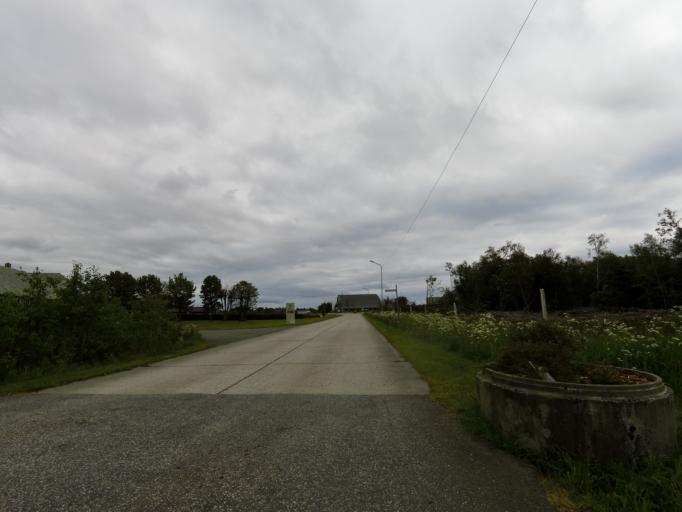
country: NO
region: Vest-Agder
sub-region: Farsund
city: Vestbygd
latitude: 58.1152
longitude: 6.6132
